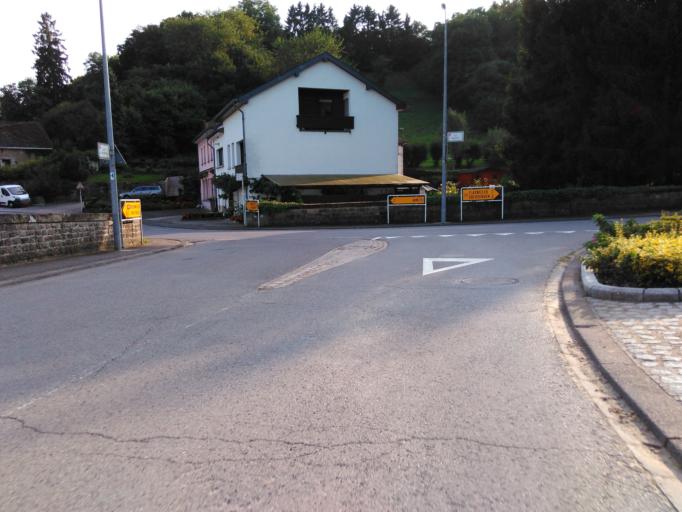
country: LU
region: Grevenmacher
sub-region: Canton de Grevenmacher
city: Wormeldange
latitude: 49.6390
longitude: 6.4054
